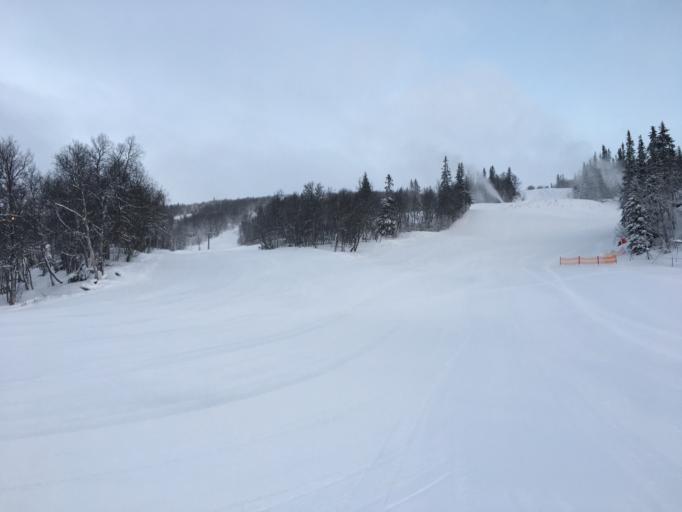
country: NO
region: Nord-Trondelag
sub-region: Meraker
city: Meraker
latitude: 63.3206
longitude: 12.0905
